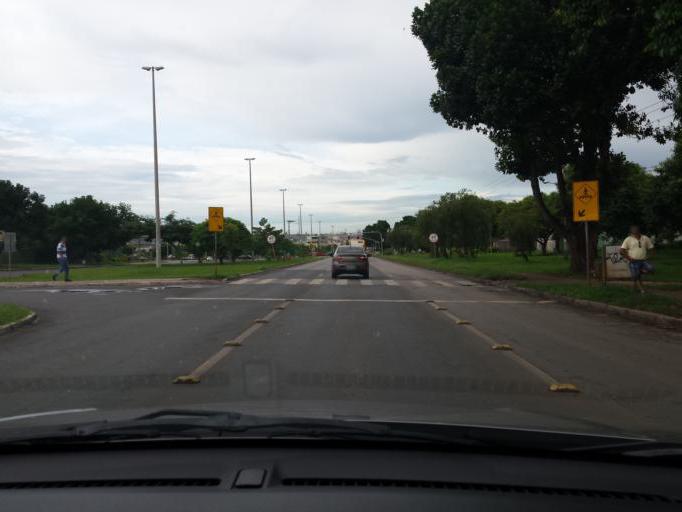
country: BR
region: Federal District
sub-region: Brasilia
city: Brasilia
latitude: -15.8463
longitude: -47.9732
